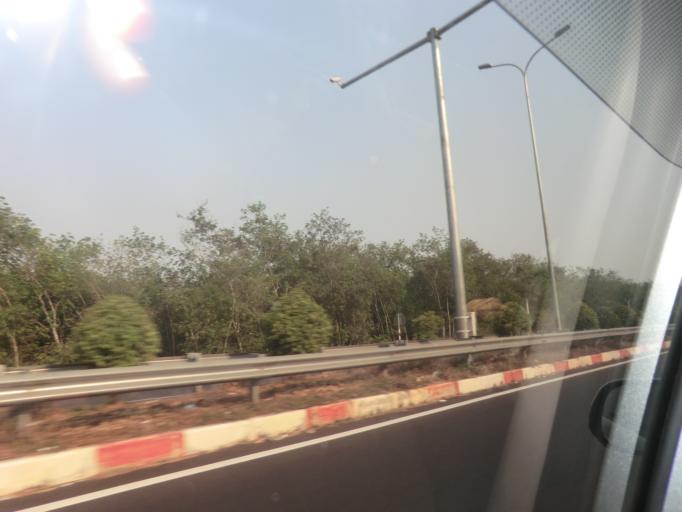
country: VN
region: Dong Nai
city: Thong Nhat
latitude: 10.9210
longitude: 107.1645
